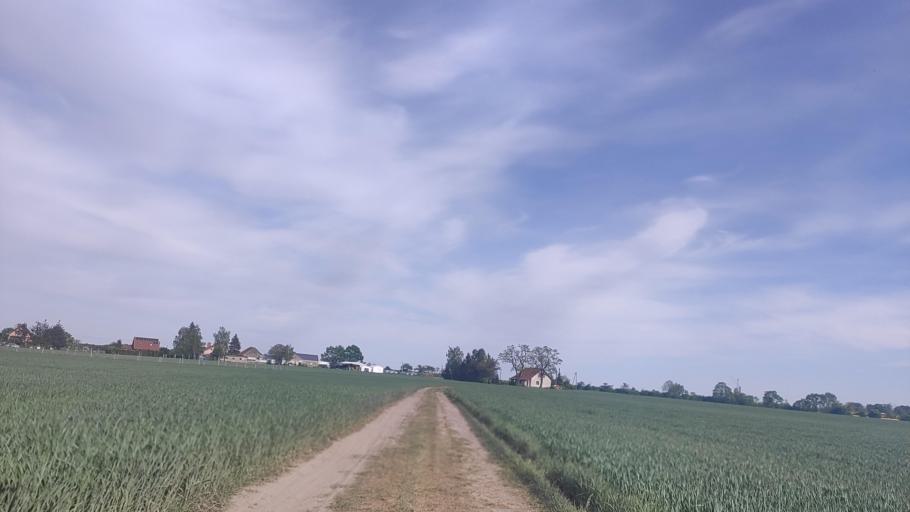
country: PL
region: Greater Poland Voivodeship
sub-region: Powiat poznanski
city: Swarzedz
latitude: 52.4158
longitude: 17.1493
